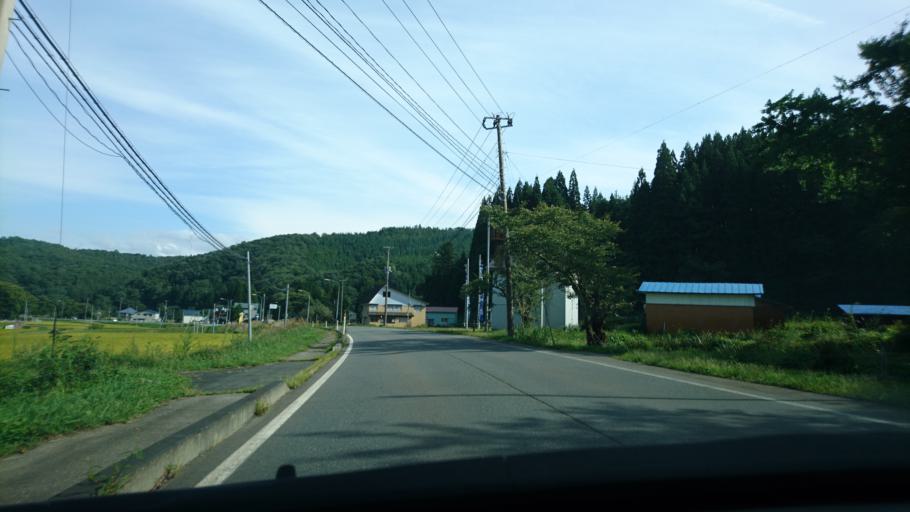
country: JP
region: Akita
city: Yokotemachi
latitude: 39.3118
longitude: 140.7593
